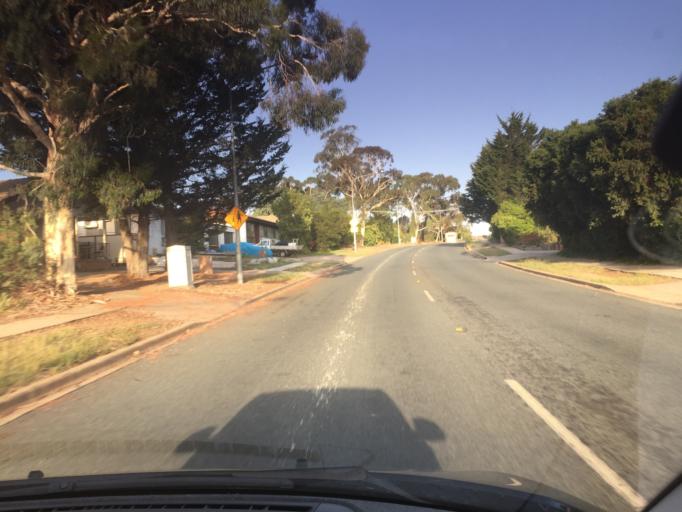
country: AU
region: Australian Capital Territory
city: Kaleen
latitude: -35.2178
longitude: 149.1069
